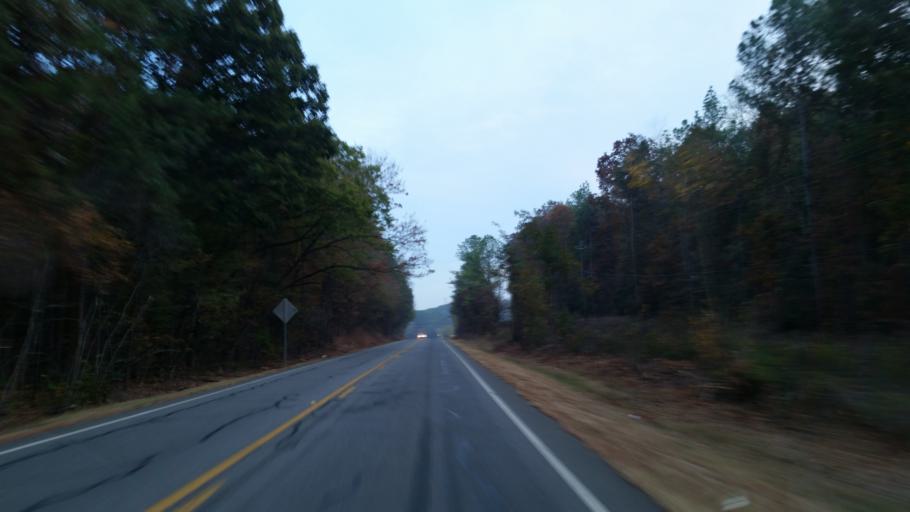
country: US
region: Georgia
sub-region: Murray County
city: Chatsworth
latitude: 34.5909
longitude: -84.7234
